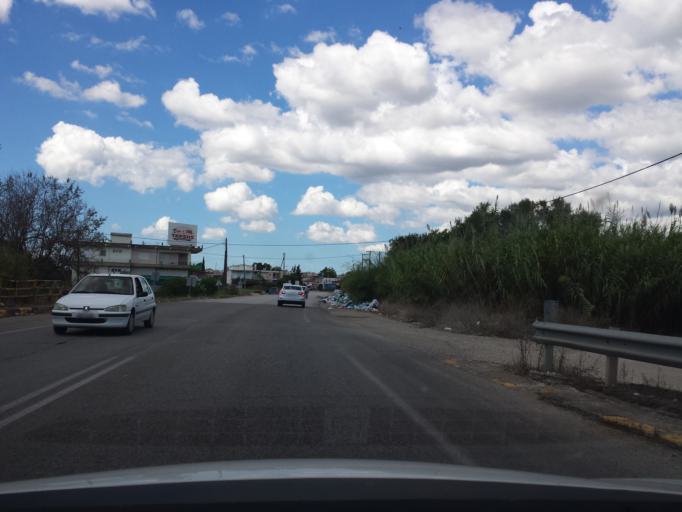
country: GR
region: West Greece
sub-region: Nomos Ileias
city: Pyrgos
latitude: 37.6632
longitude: 21.4598
